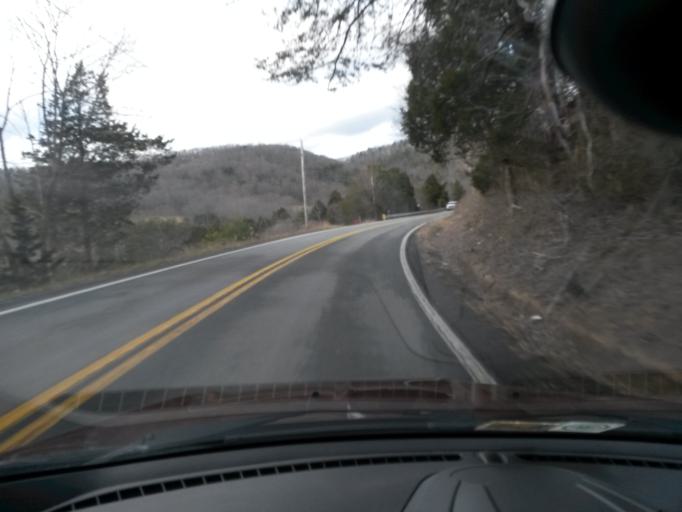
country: US
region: West Virginia
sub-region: Monroe County
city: Union
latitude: 37.4994
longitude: -80.6110
